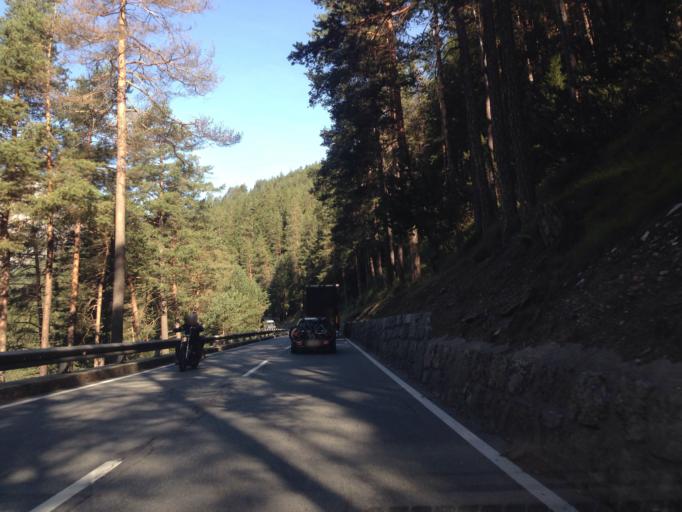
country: AT
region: Tyrol
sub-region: Politischer Bezirk Imst
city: Nassereith
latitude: 47.3540
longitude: 10.8399
